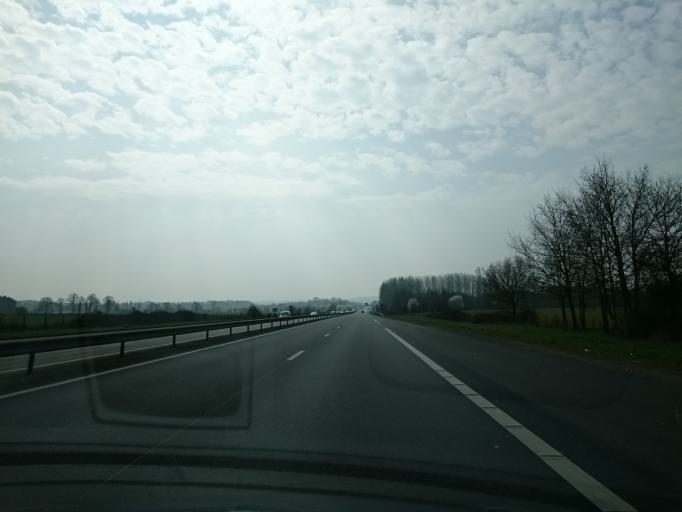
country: FR
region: Brittany
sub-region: Departement d'Ille-et-Vilaine
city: Chartres-de-Bretagne
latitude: 48.0146
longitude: -1.6915
